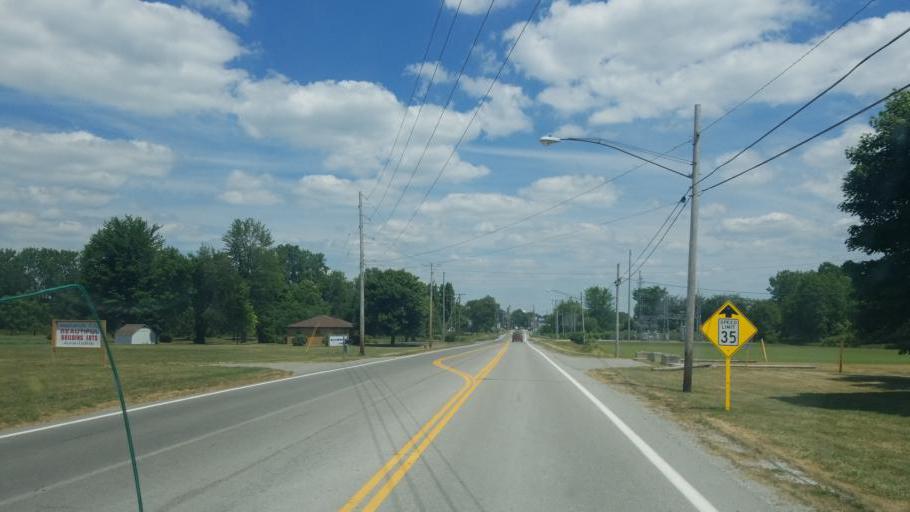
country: US
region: Ohio
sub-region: Defiance County
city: Hicksville
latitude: 41.2842
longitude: -84.7797
